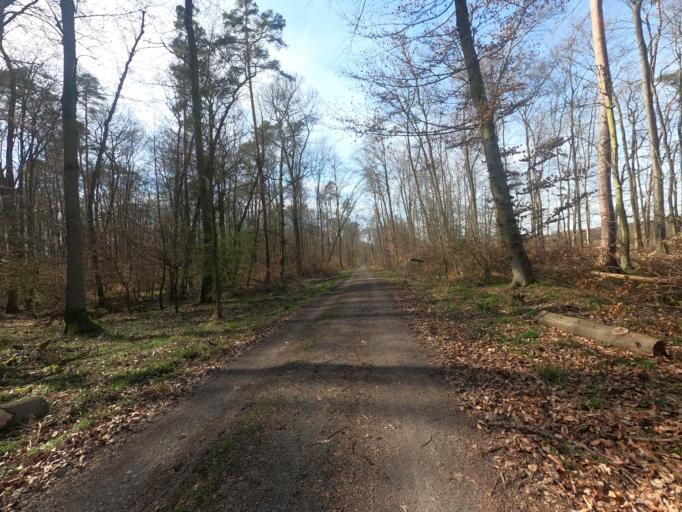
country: DE
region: Hesse
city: Morfelden-Walldorf
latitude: 49.9686
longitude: 8.5387
